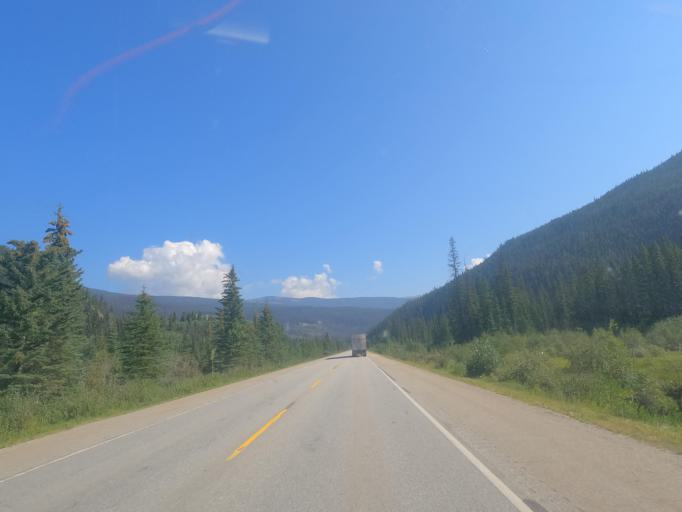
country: CA
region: Alberta
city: Jasper Park Lodge
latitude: 52.8797
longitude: -118.4915
